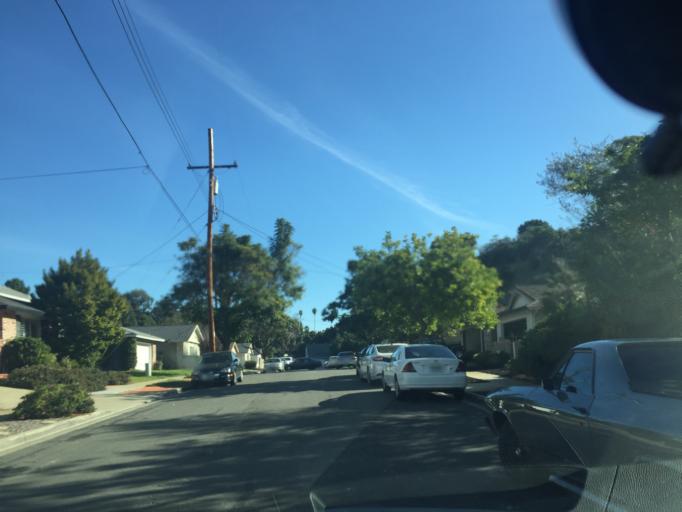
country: US
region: California
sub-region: San Diego County
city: Lemon Grove
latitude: 32.7667
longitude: -117.0797
